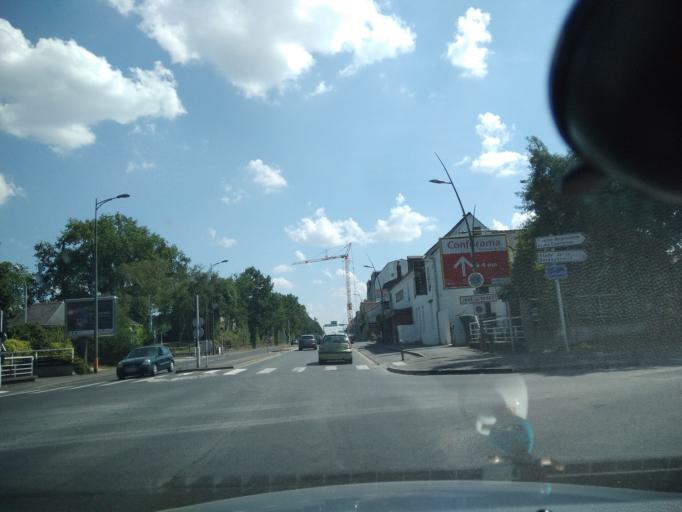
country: FR
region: Centre
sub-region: Departement d'Indre-et-Loire
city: Chambray-les-Tours
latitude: 47.3599
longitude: 0.6974
